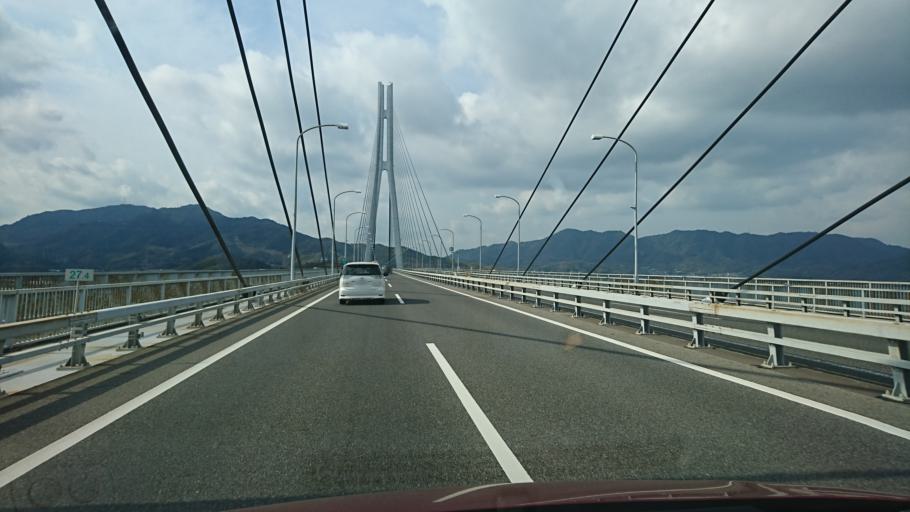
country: JP
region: Hiroshima
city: Innoshima
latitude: 34.2601
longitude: 133.0661
